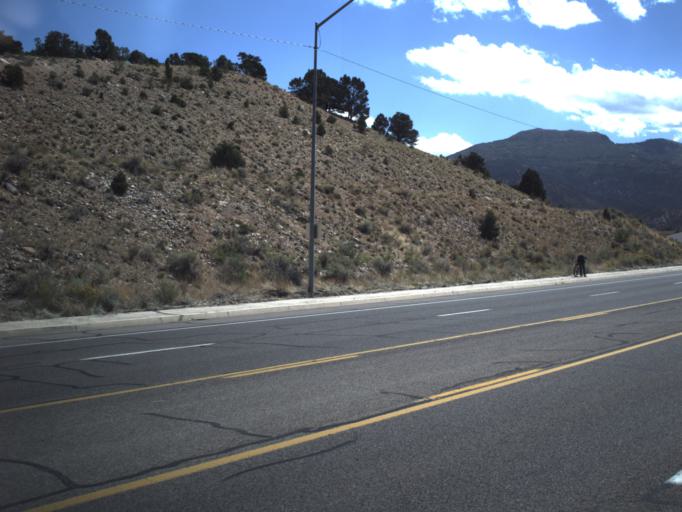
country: US
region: Utah
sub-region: Iron County
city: Cedar City
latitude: 37.6998
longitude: -113.0641
